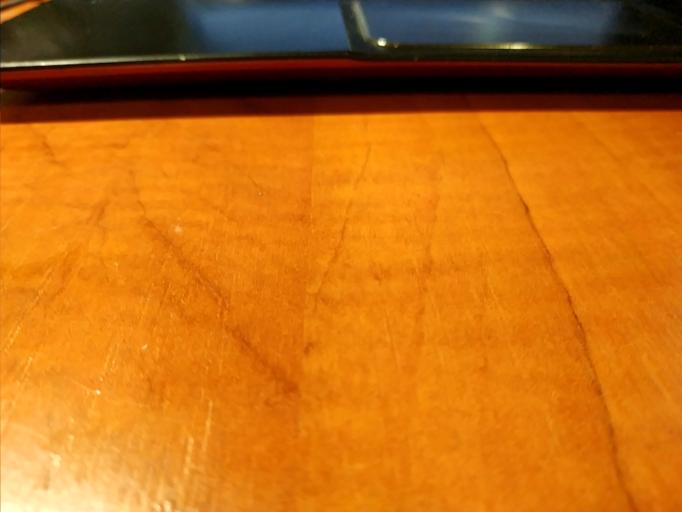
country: RU
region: Tverskaya
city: Ves'yegonsk
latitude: 58.7892
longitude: 37.5436
